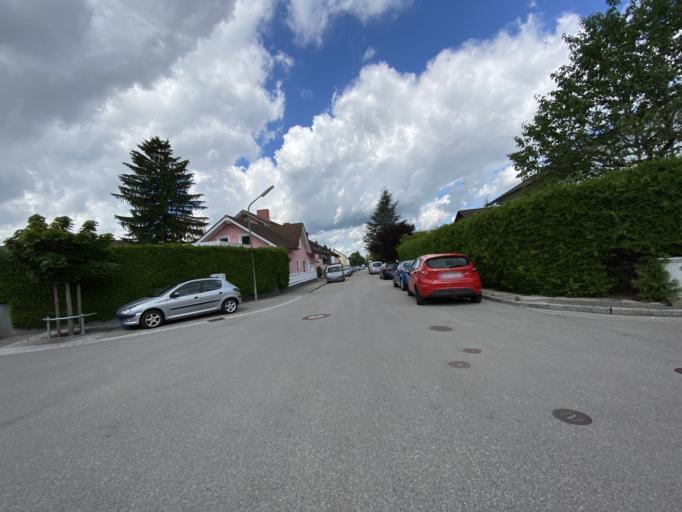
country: DE
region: Bavaria
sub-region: Upper Bavaria
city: Gilching
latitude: 48.0946
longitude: 11.2895
